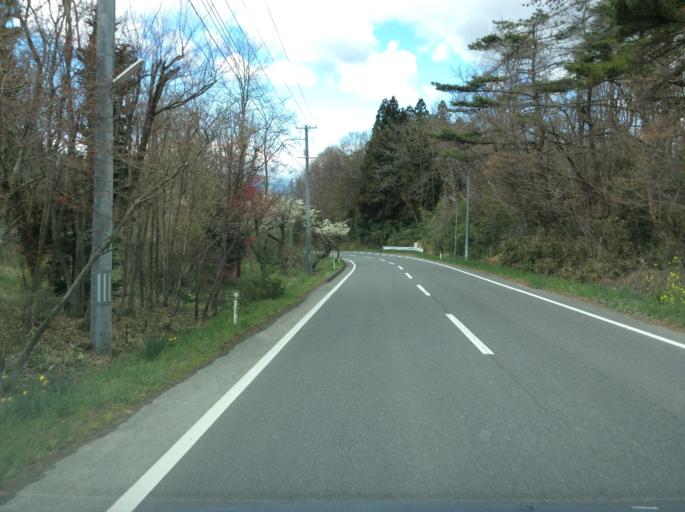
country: JP
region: Fukushima
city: Koriyama
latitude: 37.3541
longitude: 140.4109
